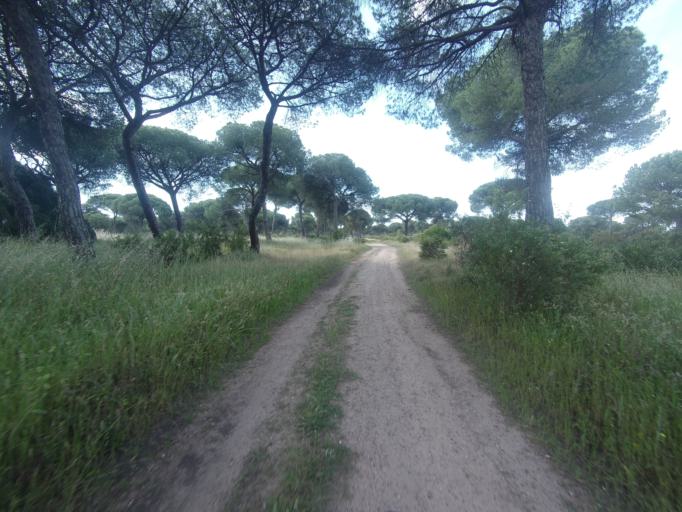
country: ES
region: Andalusia
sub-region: Provincia de Huelva
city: Aljaraque
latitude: 37.2310
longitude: -7.0628
